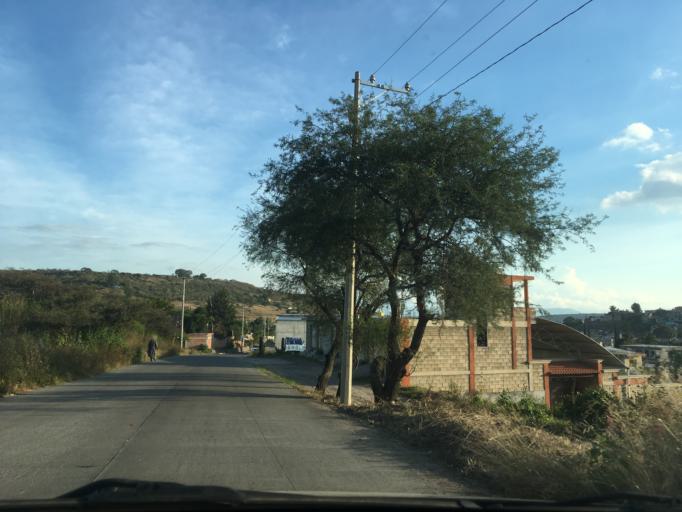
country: MX
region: Michoacan
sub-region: Cuitzeo
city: San Juan Benito Juarez (San Juan Tararameo)
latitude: 19.8752
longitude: -101.1433
